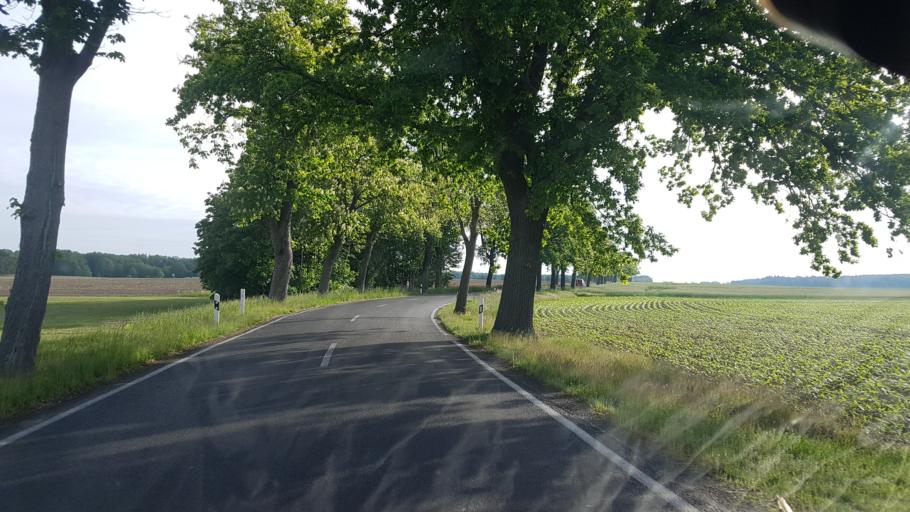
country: DE
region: Brandenburg
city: Dahme
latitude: 51.8883
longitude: 13.4637
